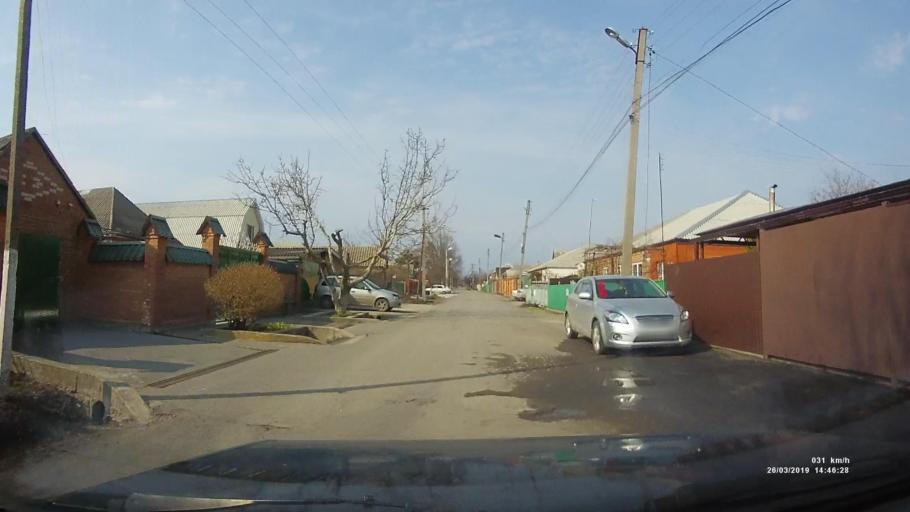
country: RU
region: Rostov
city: Novobessergenovka
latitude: 47.1867
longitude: 38.8604
